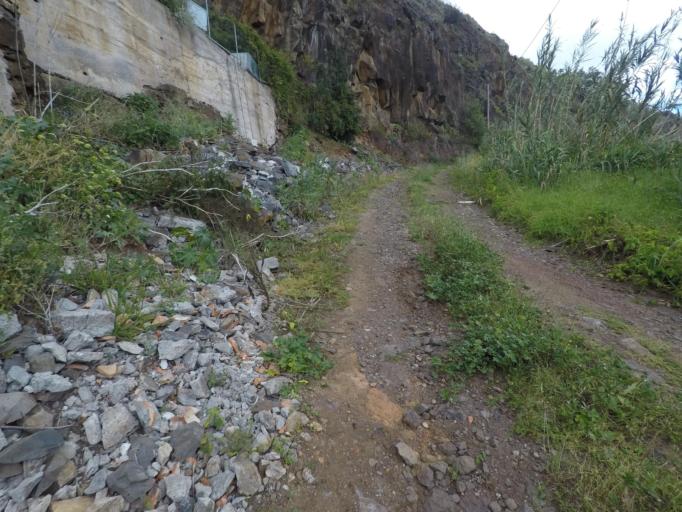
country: PT
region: Madeira
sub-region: Calheta
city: Estreito da Calheta
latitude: 32.7298
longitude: -17.1799
